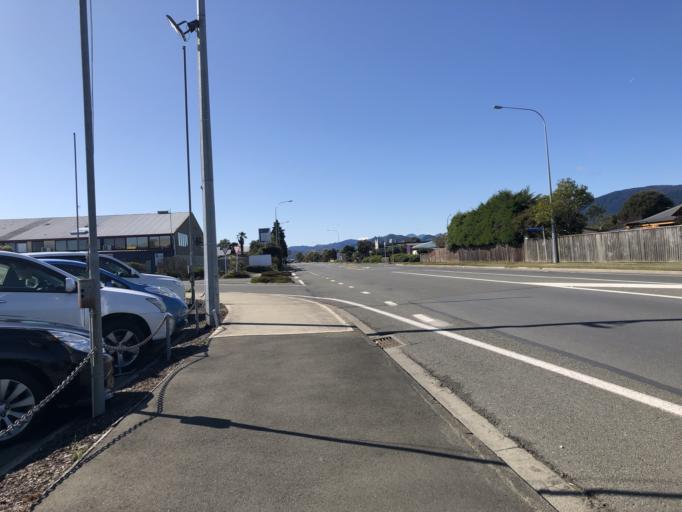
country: NZ
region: Tasman
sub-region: Tasman District
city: Richmond
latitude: -41.3427
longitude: 173.1720
